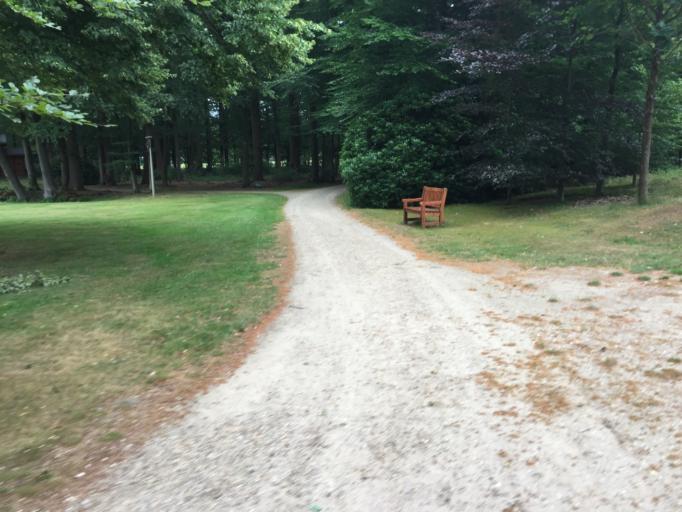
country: NL
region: Utrecht
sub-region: Gemeente Baarn
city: Baarn
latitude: 52.1938
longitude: 5.2750
